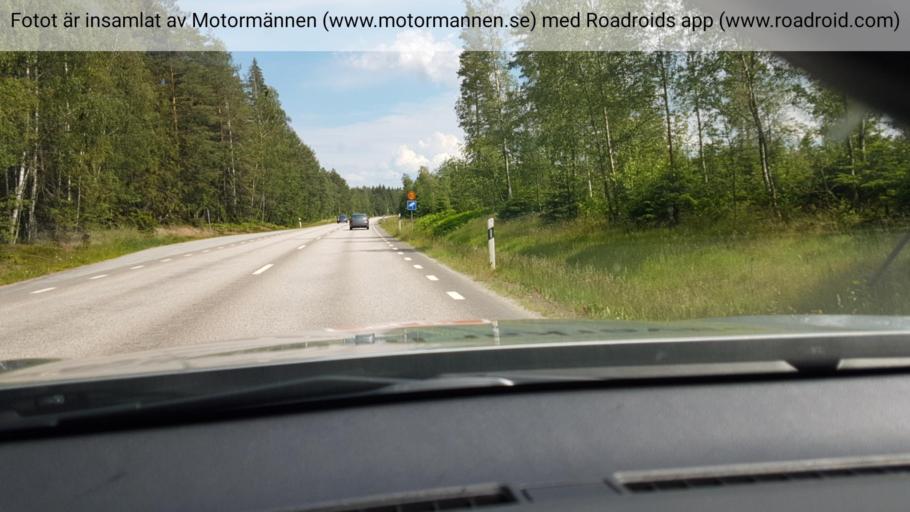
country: SE
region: Vaestra Goetaland
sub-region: Hjo Kommun
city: Hjo
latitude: 58.3409
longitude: 14.2205
